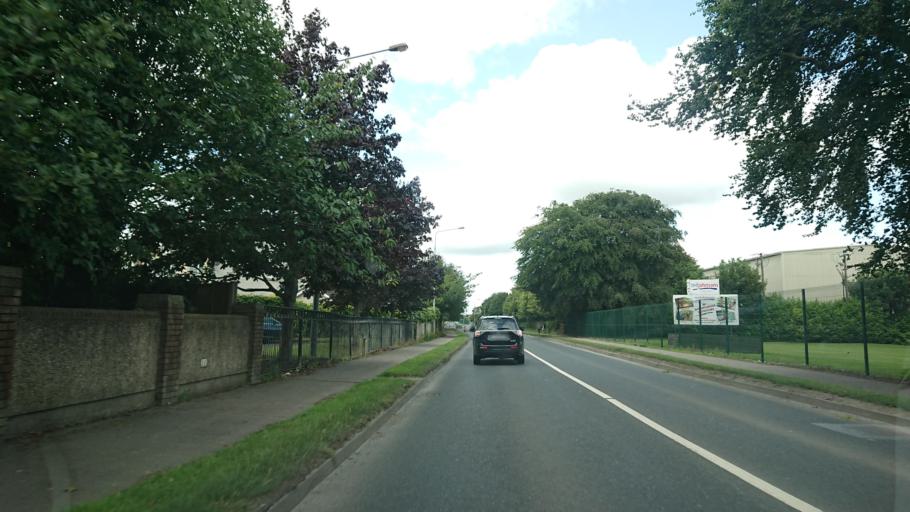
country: IE
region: Leinster
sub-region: Kildare
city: Sallins
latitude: 53.2374
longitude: -6.6535
